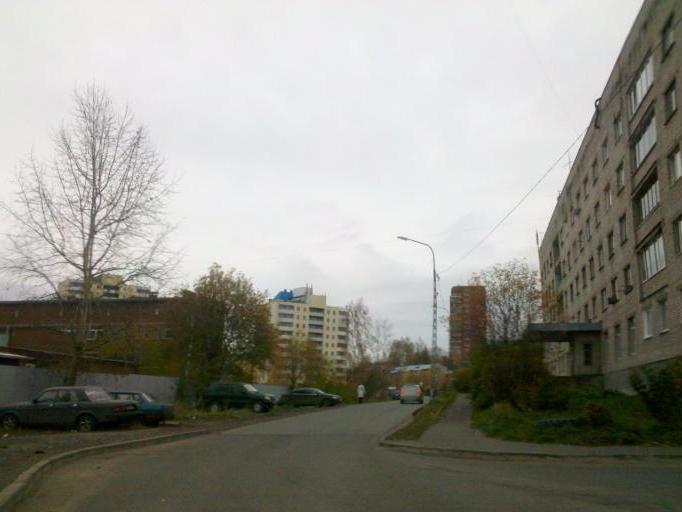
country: RU
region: Republic of Karelia
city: Petrozavodsk
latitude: 61.7757
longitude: 34.3851
